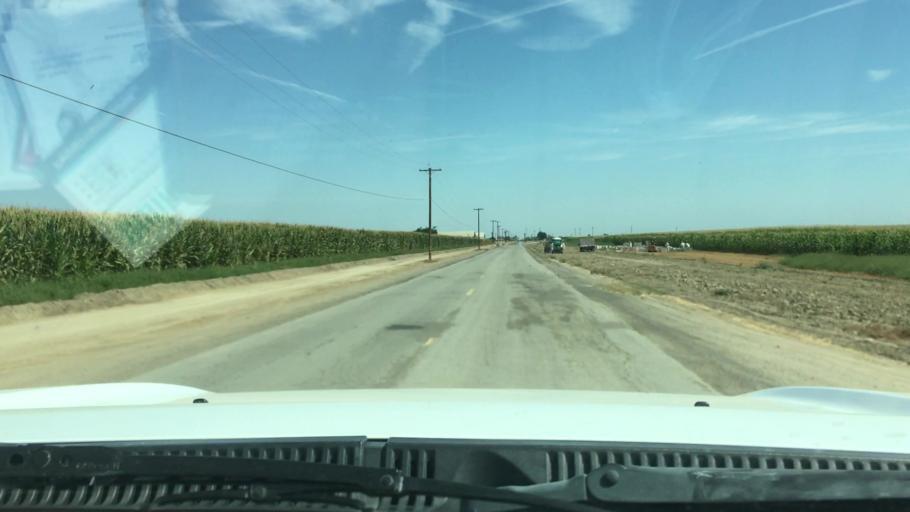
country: US
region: California
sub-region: Kern County
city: Buttonwillow
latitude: 35.4064
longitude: -119.3766
